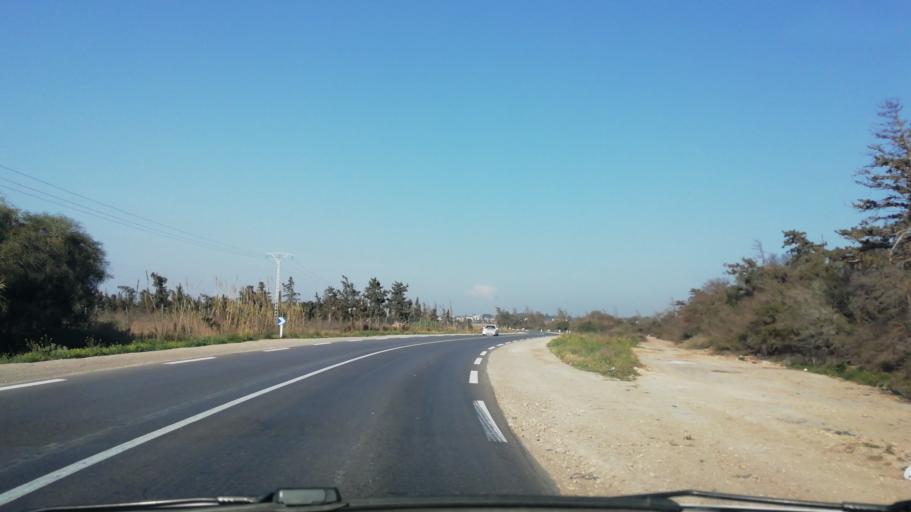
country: DZ
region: Mostaganem
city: Mostaganem
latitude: 35.7426
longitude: -0.0100
